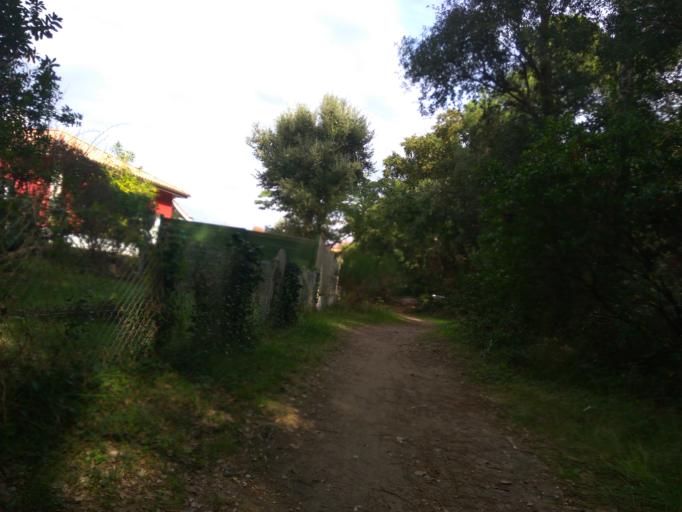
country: FR
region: Aquitaine
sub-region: Departement des Landes
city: Capbreton
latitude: 43.6328
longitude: -1.4424
